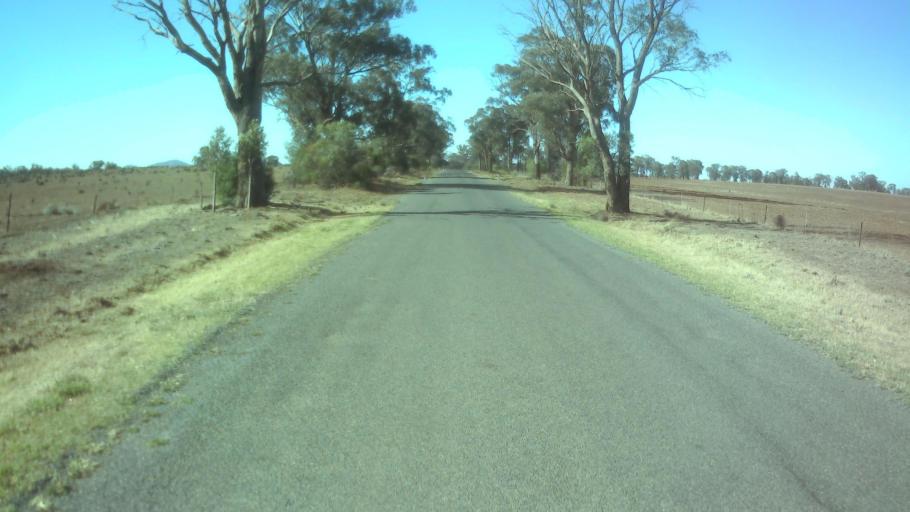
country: AU
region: New South Wales
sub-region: Forbes
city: Forbes
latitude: -33.7000
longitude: 147.8068
